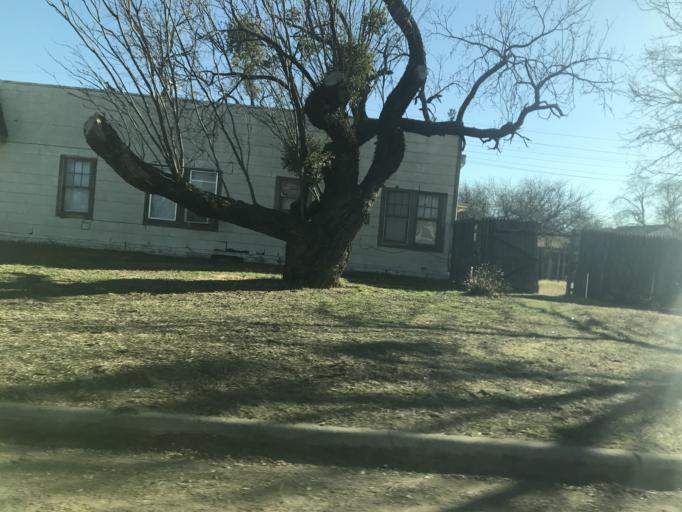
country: US
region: Texas
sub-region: Taylor County
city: Abilene
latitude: 32.4372
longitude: -99.7536
